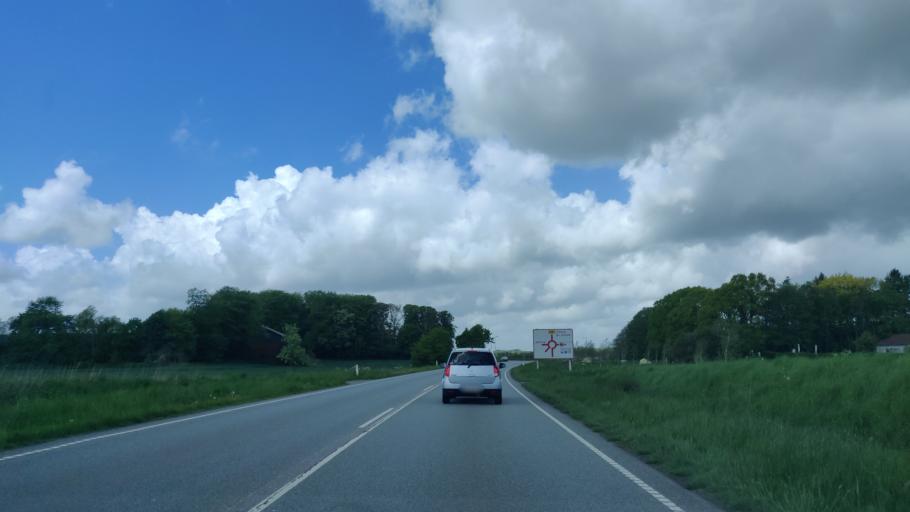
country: DK
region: Central Jutland
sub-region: Hedensted Kommune
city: Torring
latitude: 55.8468
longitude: 9.4797
